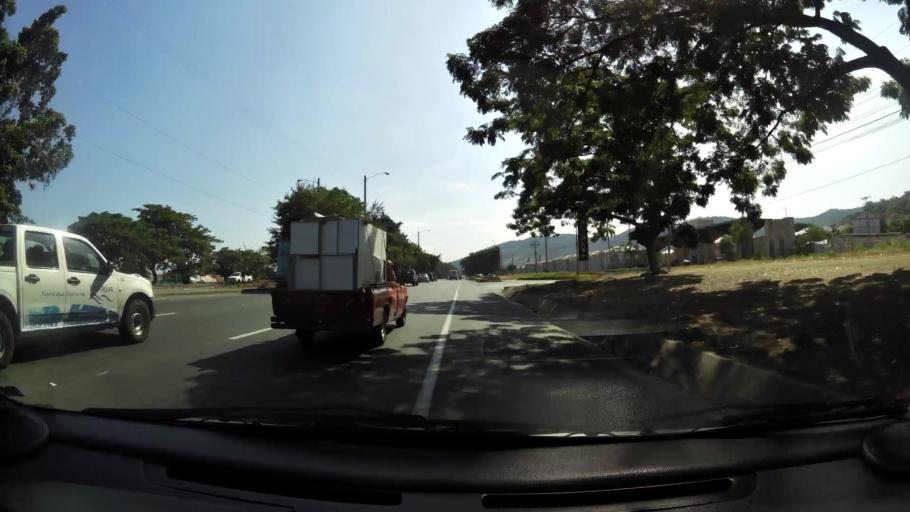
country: EC
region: Guayas
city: Santa Lucia
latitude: -2.1854
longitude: -79.9694
